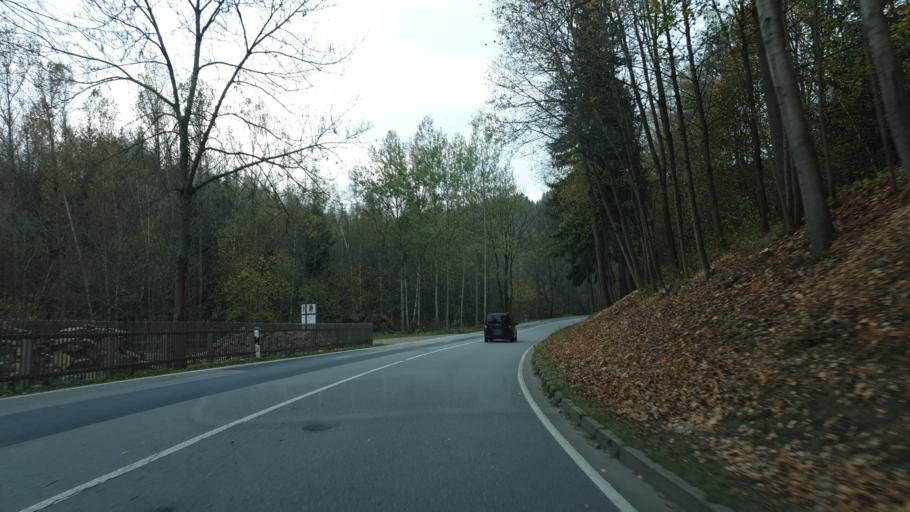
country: DE
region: Saxony
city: Breitenbrunn
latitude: 50.5054
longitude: 12.7710
